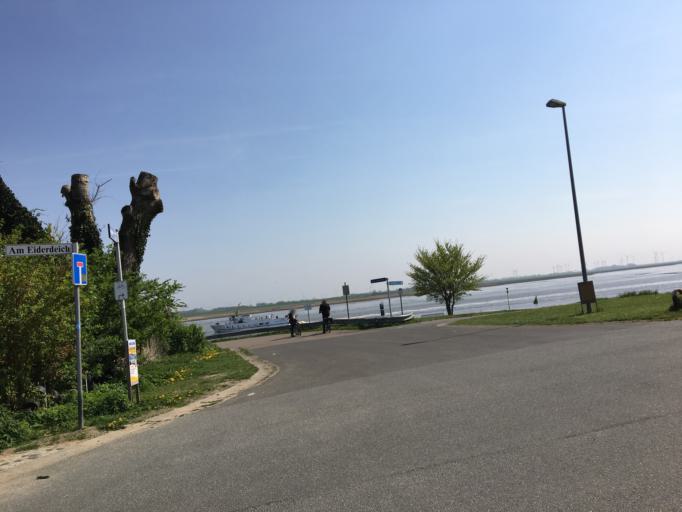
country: DE
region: Schleswig-Holstein
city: Tonning
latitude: 54.3137
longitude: 8.9442
